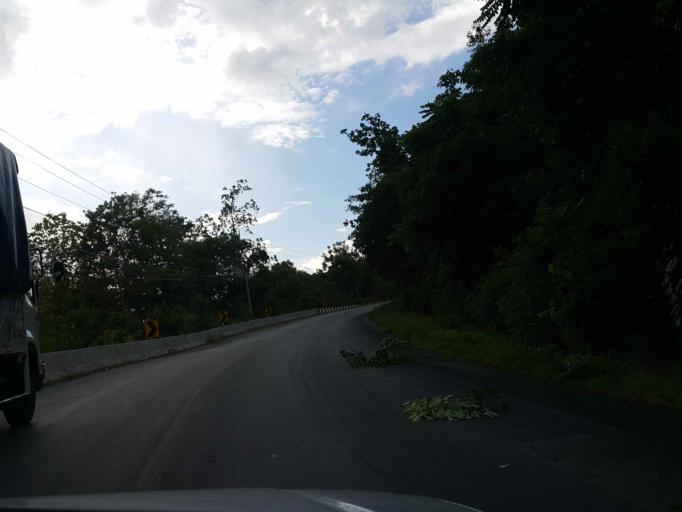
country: TH
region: Lampang
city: Thoen
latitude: 17.6138
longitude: 99.3214
